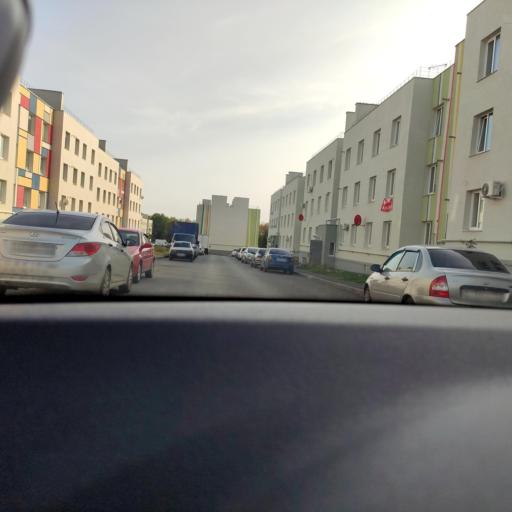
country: RU
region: Samara
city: Petra-Dubrava
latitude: 53.3034
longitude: 50.3432
